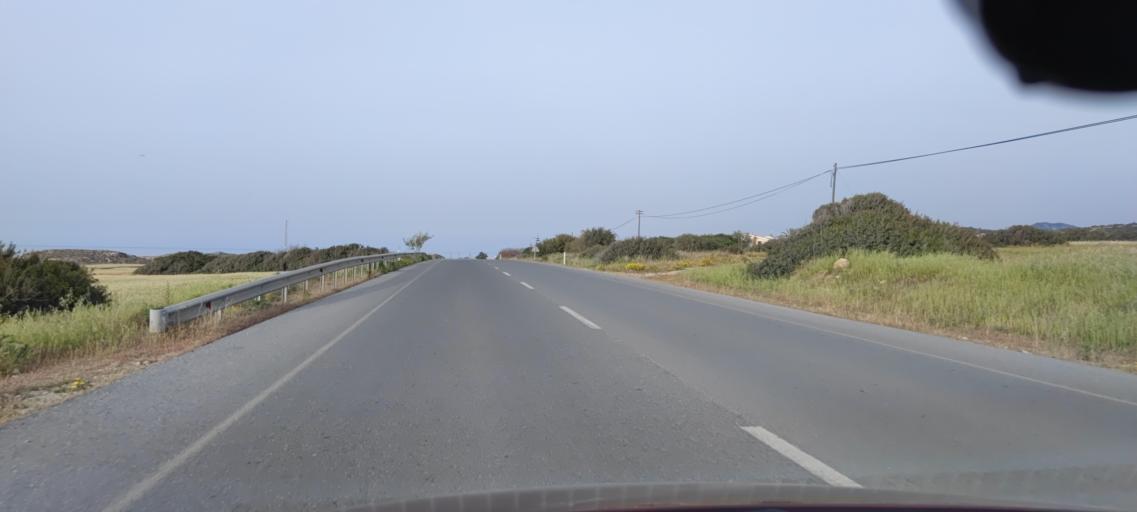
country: CY
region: Ammochostos
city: Leonarisso
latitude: 35.5614
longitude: 34.2435
